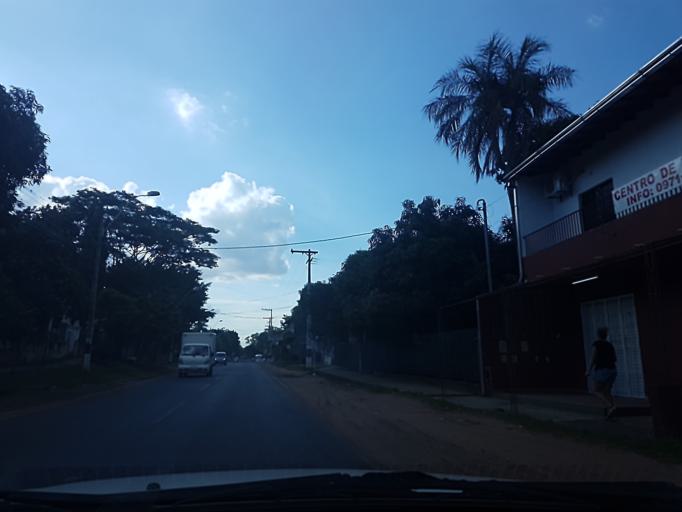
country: PY
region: Central
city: Aregua
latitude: -25.3101
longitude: -57.3808
